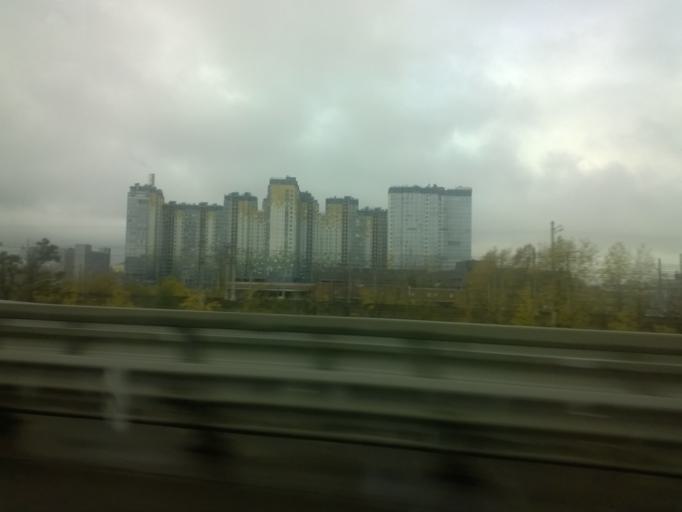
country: RU
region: St.-Petersburg
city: Avtovo
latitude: 59.8502
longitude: 30.2893
